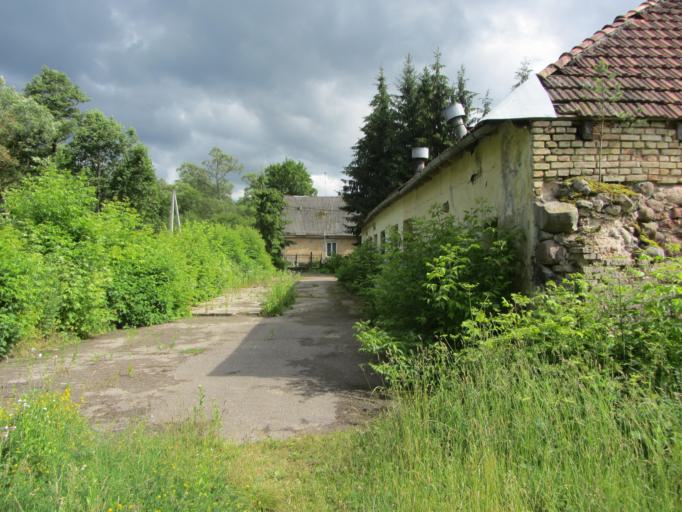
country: LT
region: Vilnius County
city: Rasos
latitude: 54.6900
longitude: 25.3555
